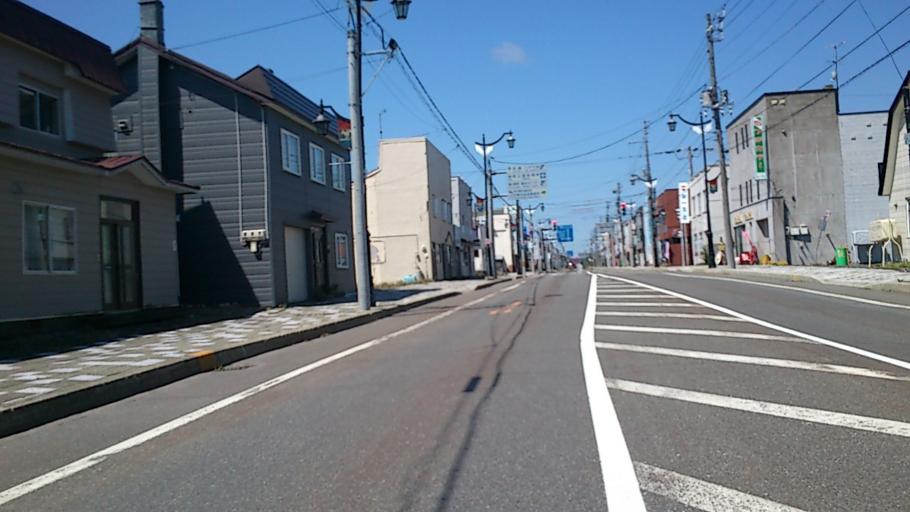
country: JP
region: Hokkaido
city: Makubetsu
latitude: 45.1252
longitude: 142.3655
